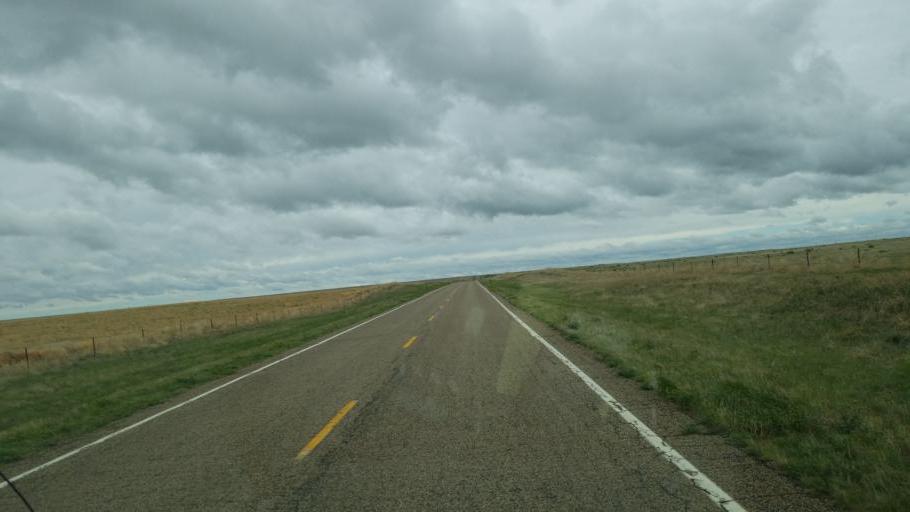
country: US
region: Colorado
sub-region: Lincoln County
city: Hugo
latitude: 38.8509
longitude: -103.6050
